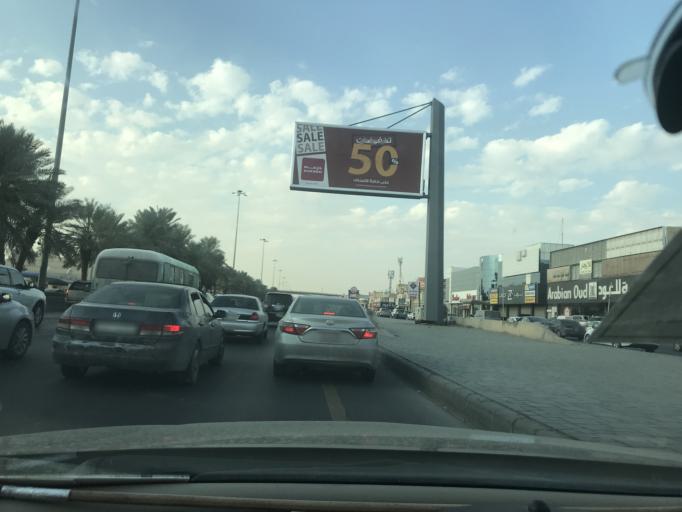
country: SA
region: Ar Riyad
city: Riyadh
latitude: 24.7536
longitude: 46.7422
